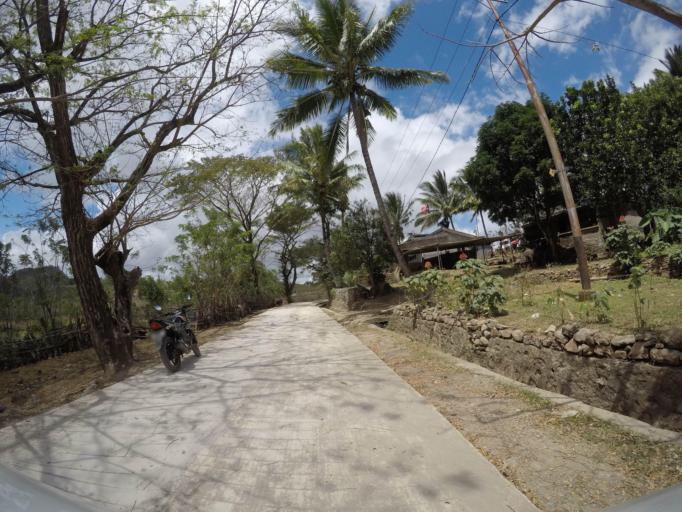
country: TL
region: Lautem
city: Lospalos
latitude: -8.5530
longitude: 126.8289
